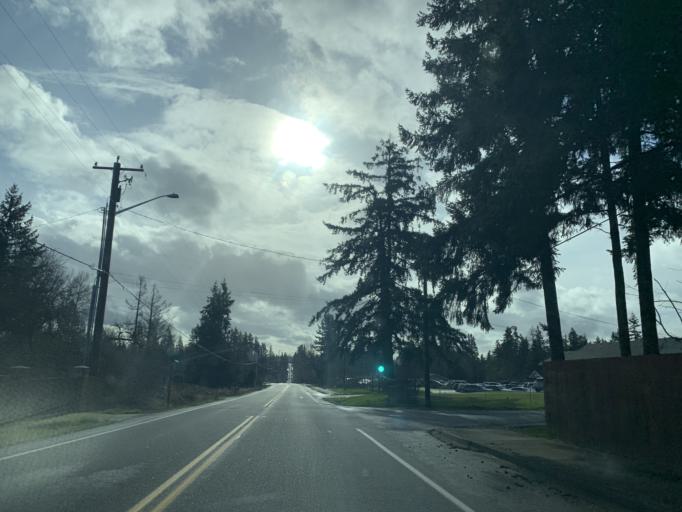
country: US
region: Washington
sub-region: Pierce County
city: Edgewood
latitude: 47.2661
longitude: -122.2979
